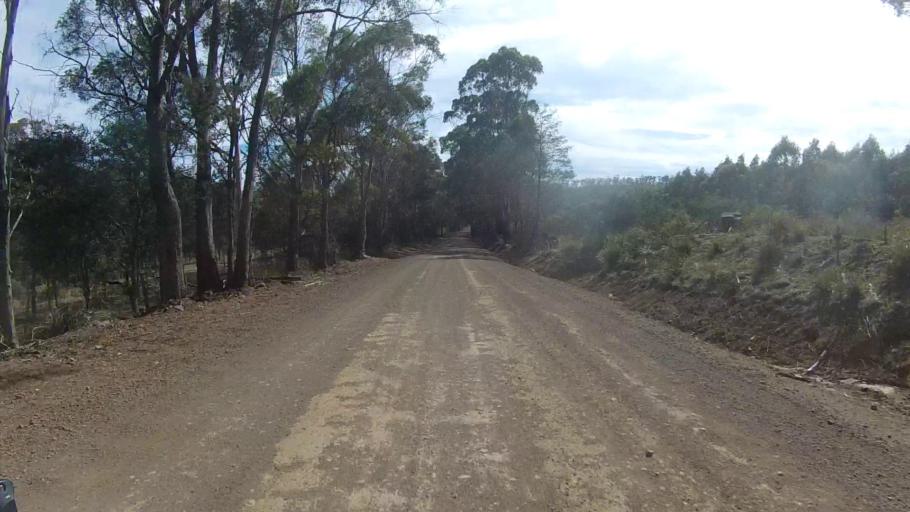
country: AU
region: Tasmania
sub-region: Sorell
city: Sorell
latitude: -42.6654
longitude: 147.8889
